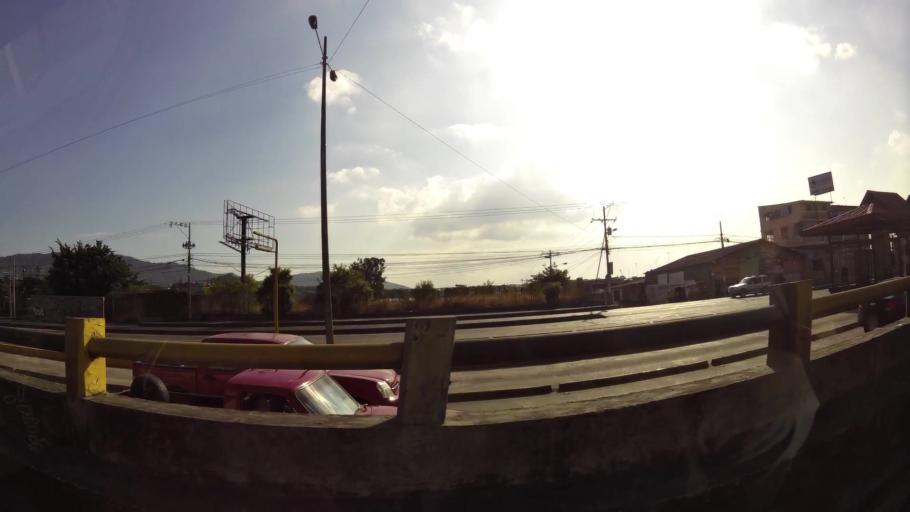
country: EC
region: Guayas
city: Guayaquil
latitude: -2.1436
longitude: -79.9343
